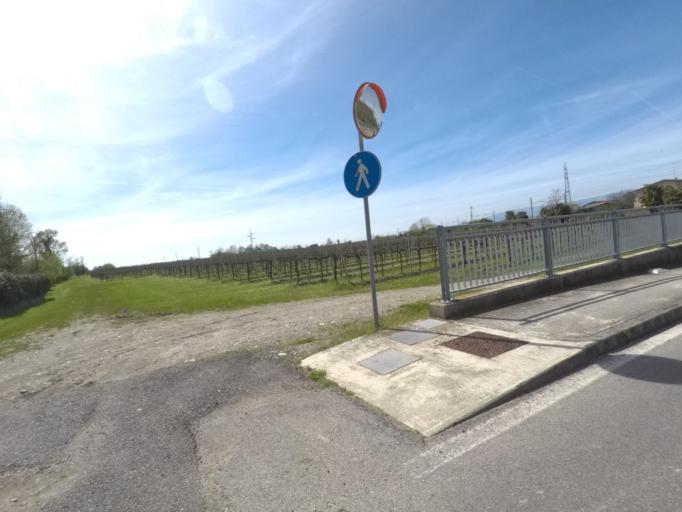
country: IT
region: Friuli Venezia Giulia
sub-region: Provincia di Pordenone
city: Castions
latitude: 45.9482
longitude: 12.7970
